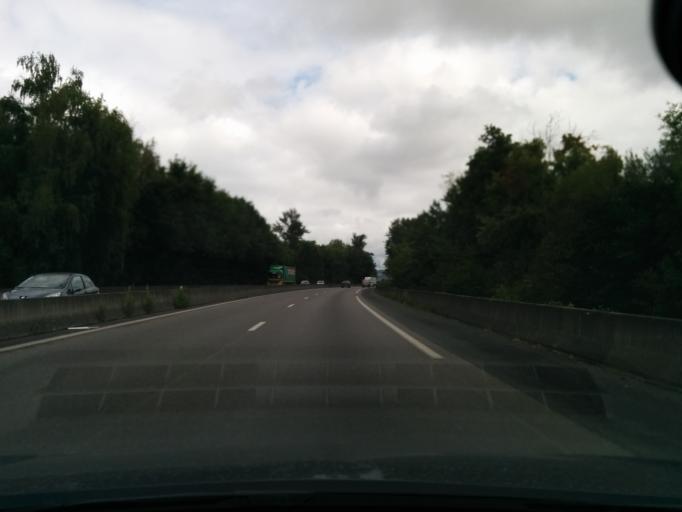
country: FR
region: Limousin
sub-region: Departement de la Correze
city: Ussac
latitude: 45.1898
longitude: 1.4935
